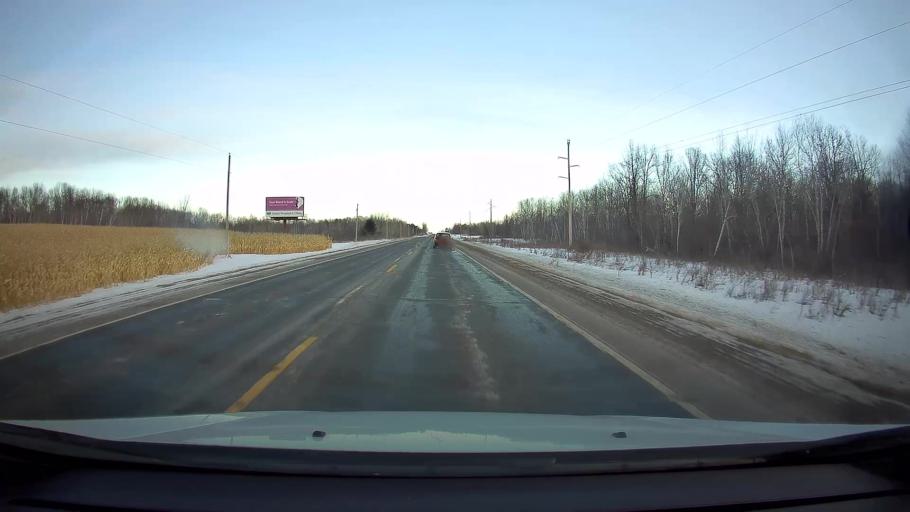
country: US
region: Wisconsin
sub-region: Barron County
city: Turtle Lake
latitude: 45.3552
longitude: -92.1669
